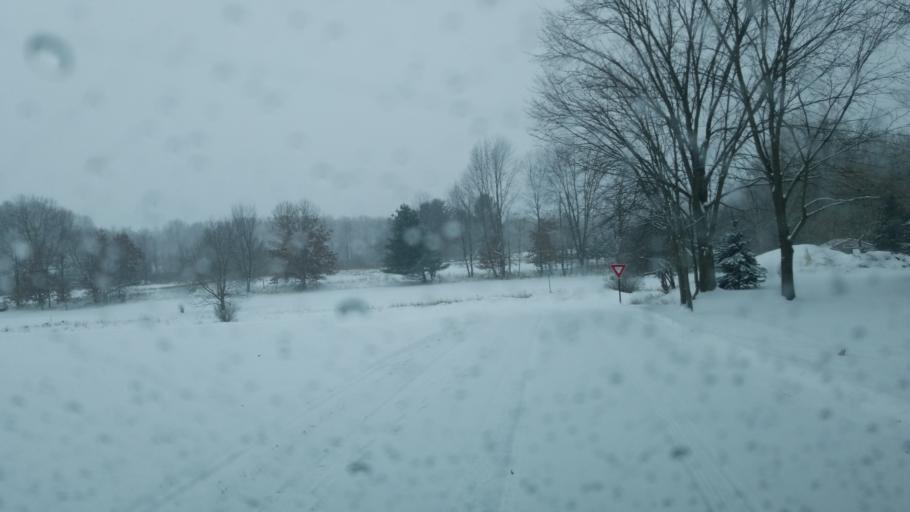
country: US
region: Michigan
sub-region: Osceola County
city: Reed City
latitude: 43.8500
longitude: -85.4469
